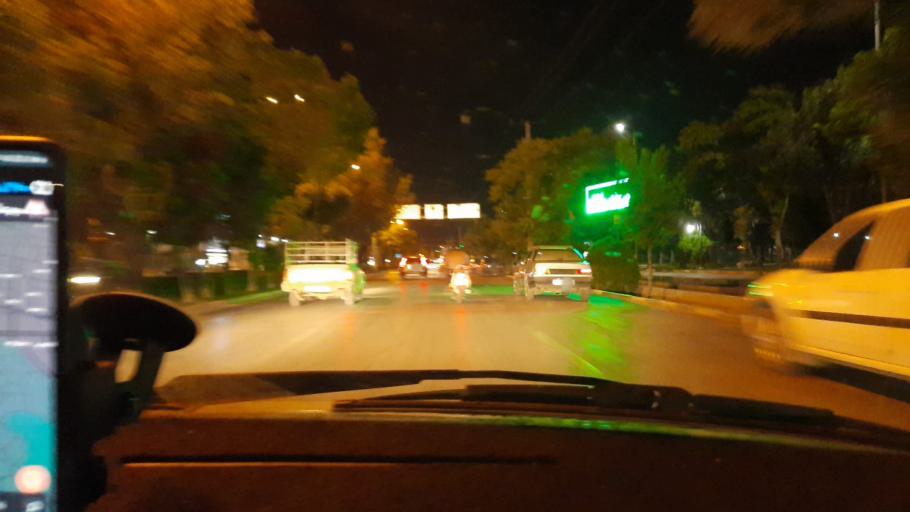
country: IR
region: Markazi
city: Arak
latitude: 34.1075
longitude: 49.6972
